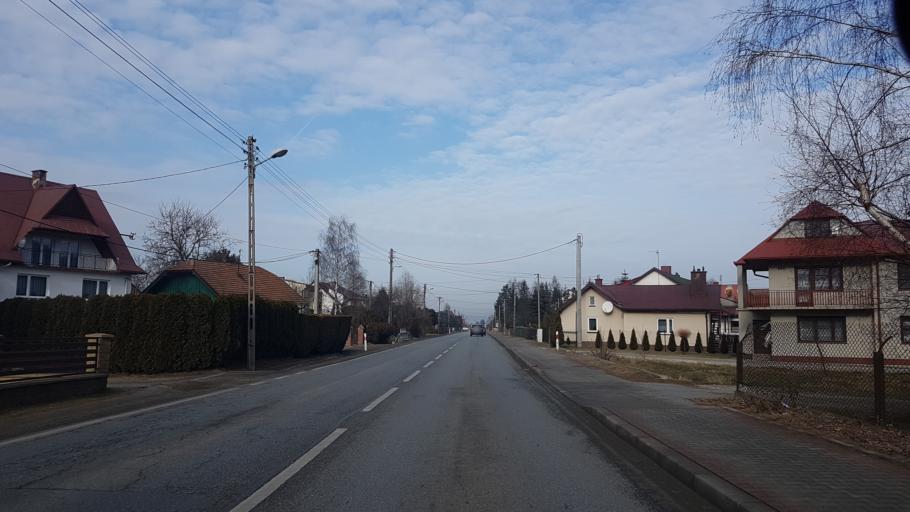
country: PL
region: Lesser Poland Voivodeship
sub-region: Powiat nowosadecki
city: Stary Sacz
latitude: 49.5306
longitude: 20.6497
